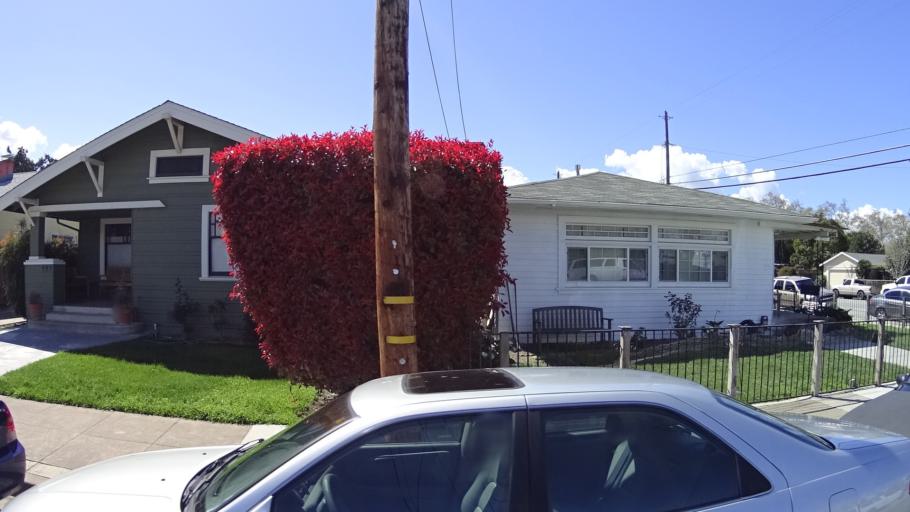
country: US
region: California
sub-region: Santa Clara County
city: San Jose
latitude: 37.3519
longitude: -121.8817
